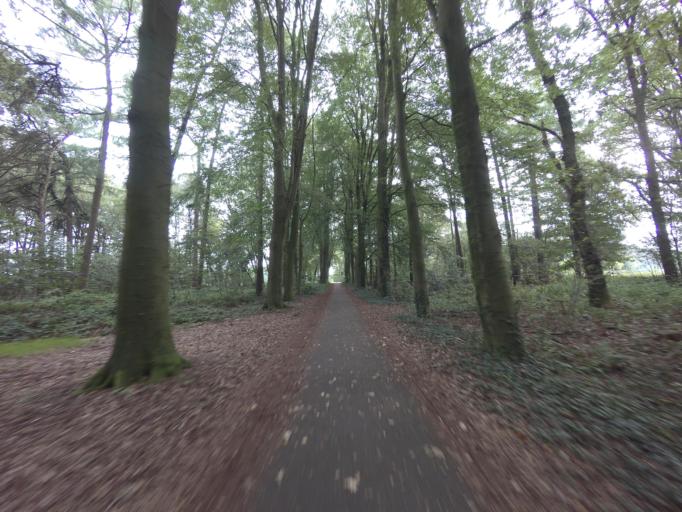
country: NL
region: Drenthe
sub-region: Gemeente Assen
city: Assen
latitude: 52.9108
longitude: 6.5196
